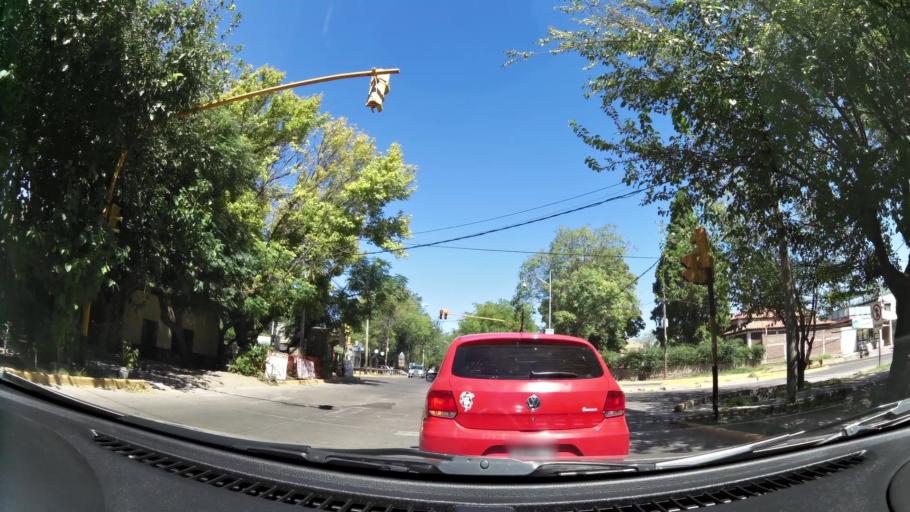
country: AR
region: Mendoza
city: Las Heras
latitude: -32.8526
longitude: -68.8465
